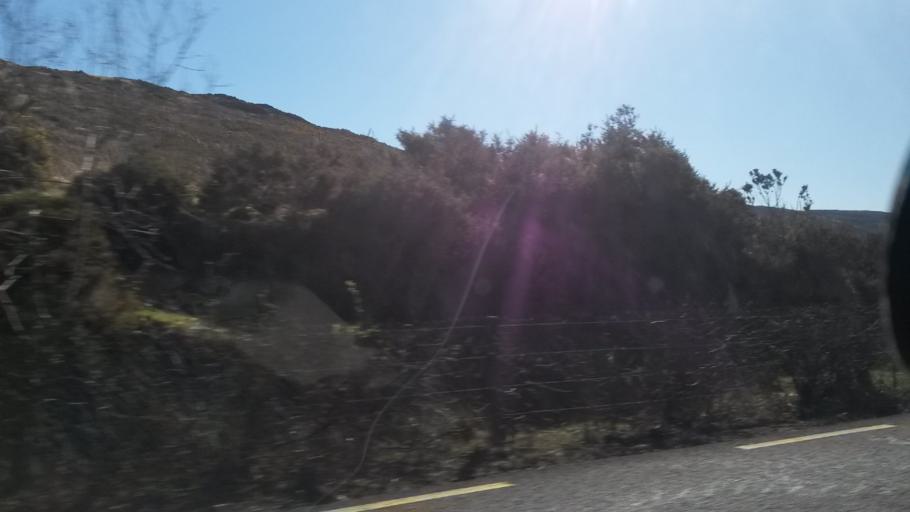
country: IE
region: Munster
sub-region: Ciarrai
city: Cill Airne
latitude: 51.9482
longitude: -9.3886
